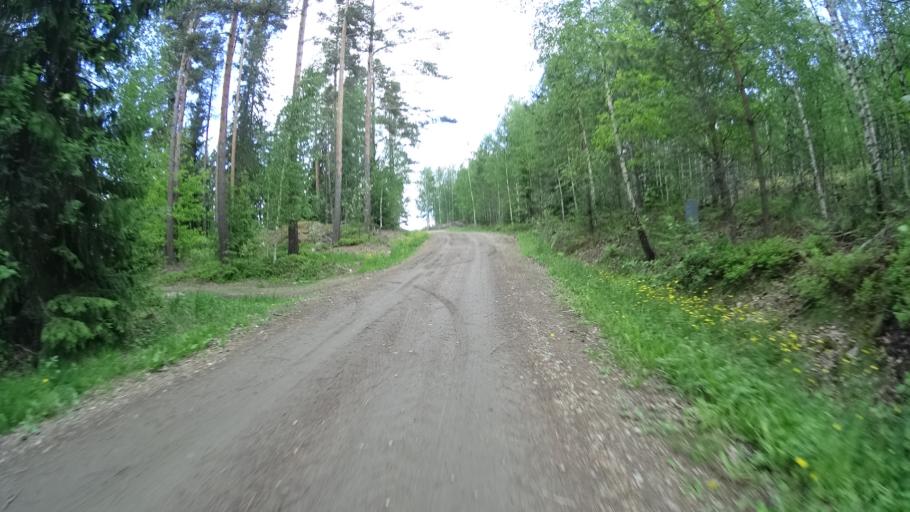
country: FI
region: Uusimaa
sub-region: Raaseporin
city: Karis
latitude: 60.1442
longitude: 23.6192
